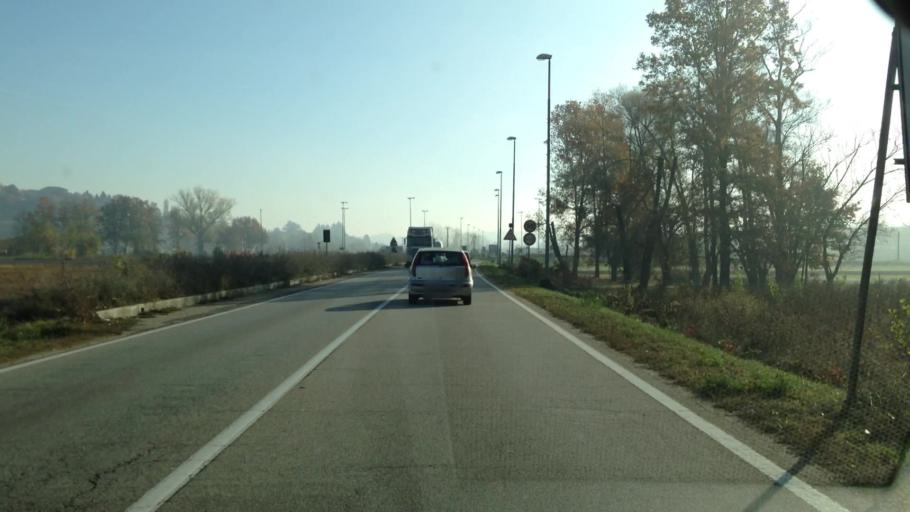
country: IT
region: Piedmont
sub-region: Provincia di Asti
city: Vigliano d'Asti
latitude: 44.8232
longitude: 8.2230
